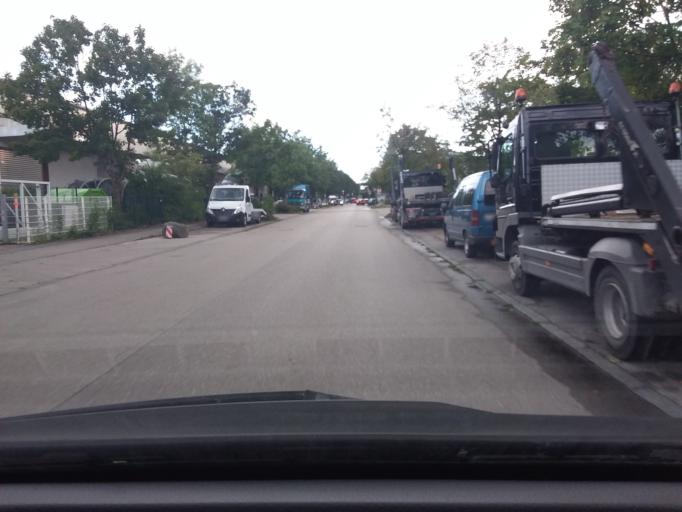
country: DE
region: Bavaria
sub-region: Upper Bavaria
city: Garching bei Munchen
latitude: 48.2518
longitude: 11.6201
